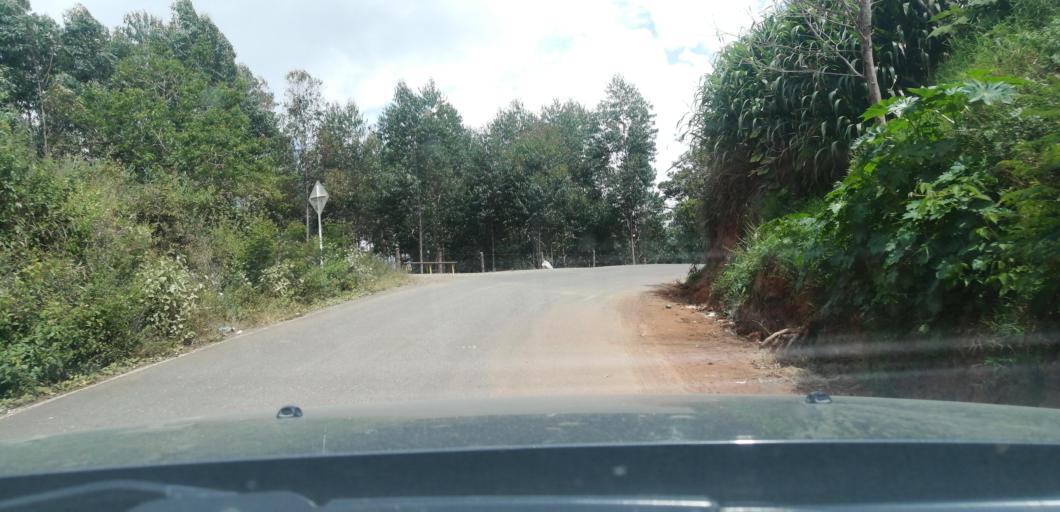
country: CO
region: Valle del Cauca
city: Dagua
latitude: 3.7101
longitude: -76.5857
